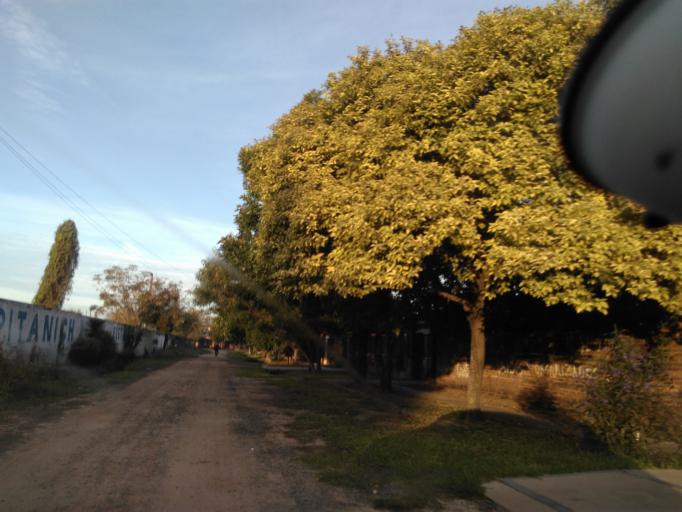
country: AR
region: Chaco
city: Resistencia
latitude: -27.4643
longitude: -59.0036
